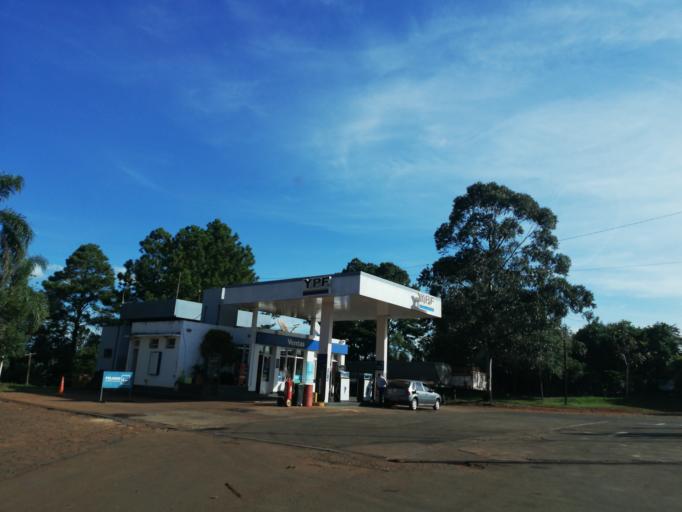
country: AR
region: Misiones
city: Dos de Mayo
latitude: -27.0041
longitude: -54.5012
